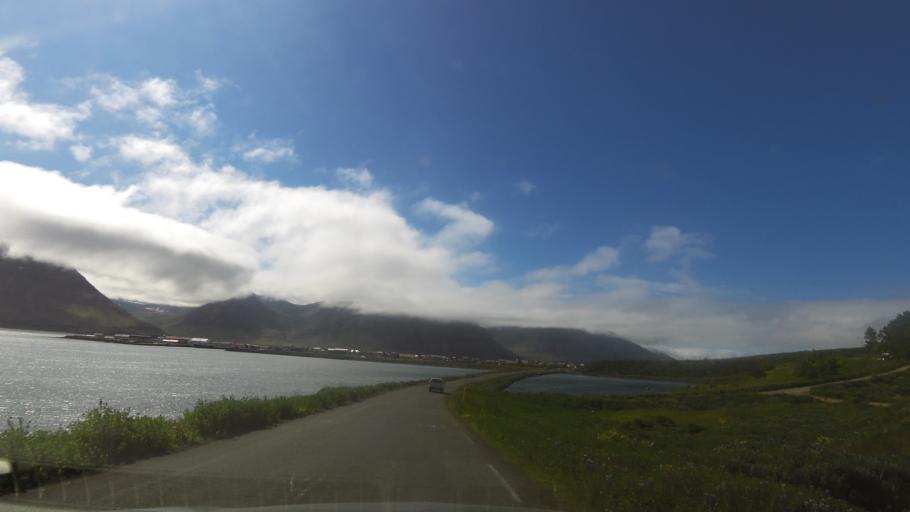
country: IS
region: Westfjords
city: Isafjoerdur
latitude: 66.0516
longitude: -23.4985
